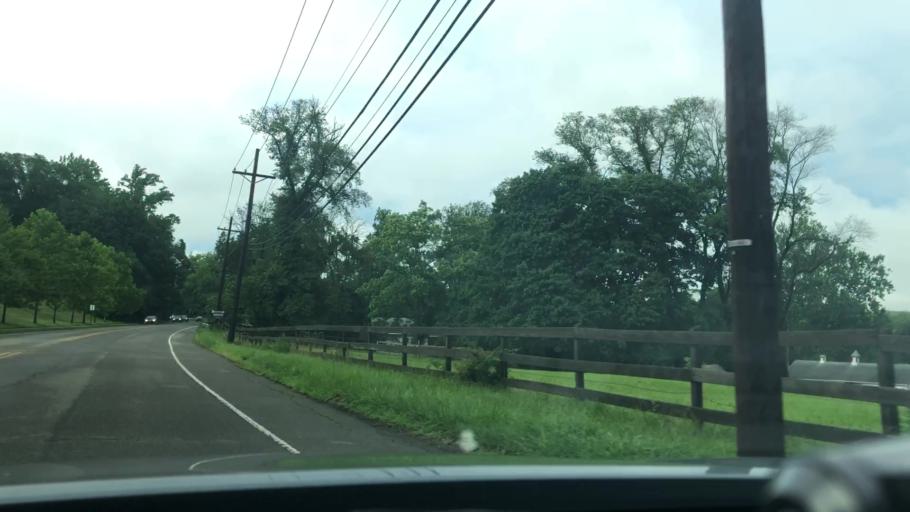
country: US
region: New Jersey
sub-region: Bergen County
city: Woodcliff Lake
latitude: 41.0182
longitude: -74.0701
